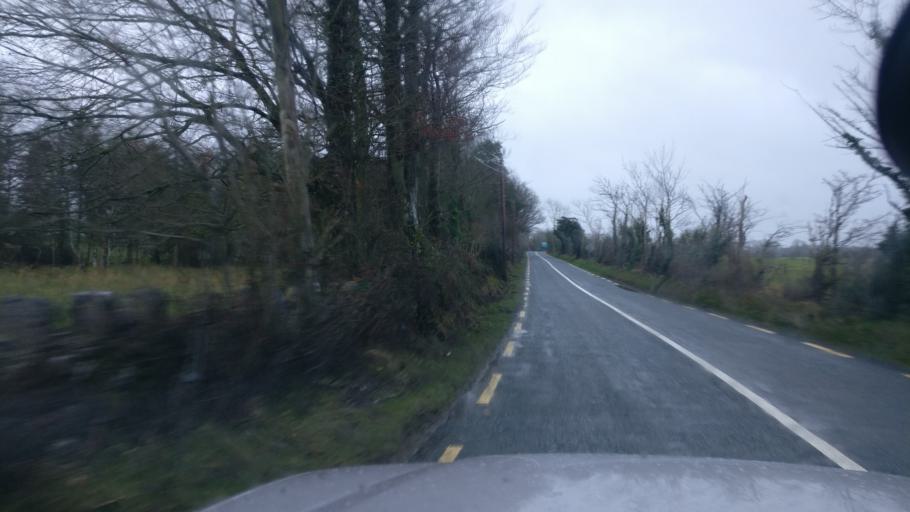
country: IE
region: Connaught
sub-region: County Galway
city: Ballinasloe
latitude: 53.2328
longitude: -8.1903
